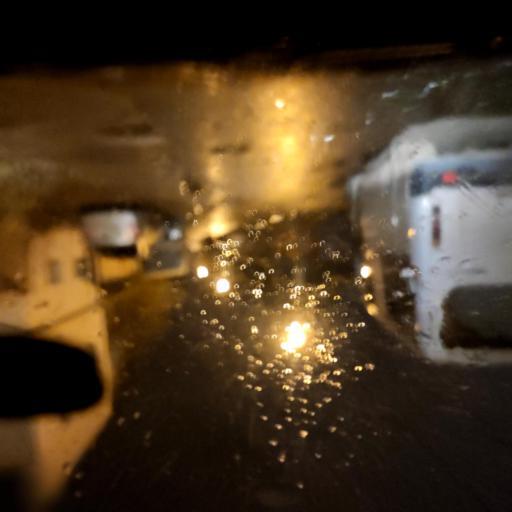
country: RU
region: Bashkortostan
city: Ufa
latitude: 54.7361
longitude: 55.8996
